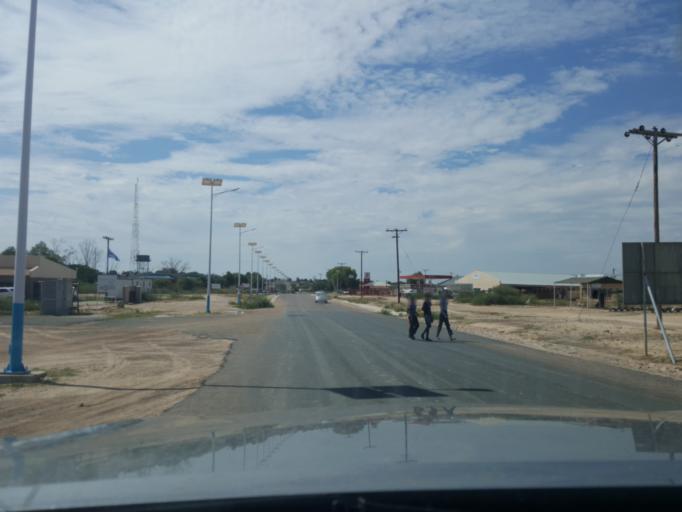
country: BW
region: Kweneng
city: Letlhakeng
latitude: -24.0986
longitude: 25.0295
